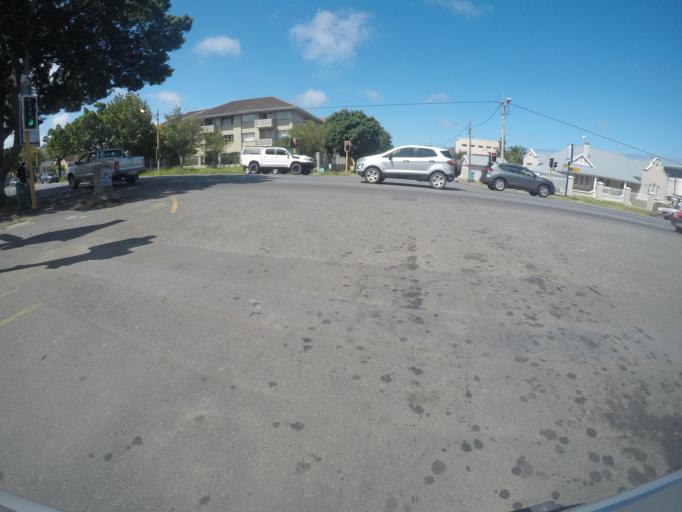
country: ZA
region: Eastern Cape
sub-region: Buffalo City Metropolitan Municipality
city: East London
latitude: -33.0018
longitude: 27.8990
